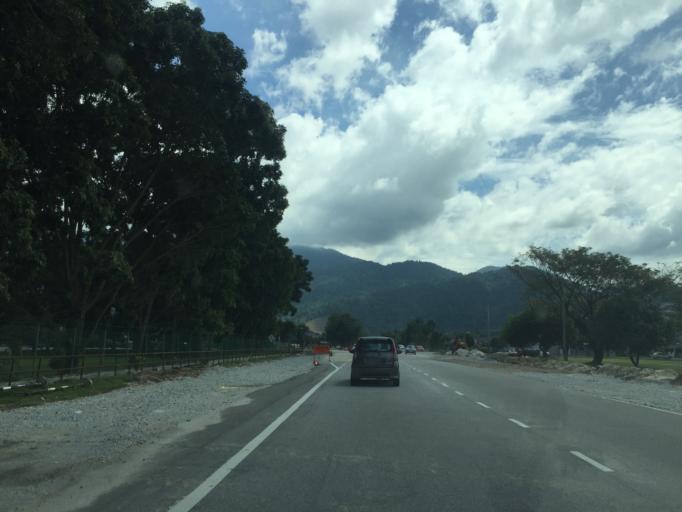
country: MY
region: Perak
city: Kampar
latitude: 4.3268
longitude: 101.1387
